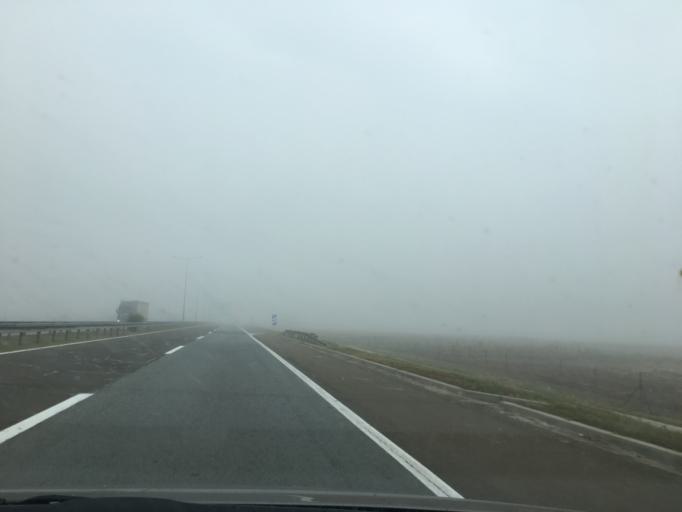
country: RS
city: Novi Karlovci
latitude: 45.0664
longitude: 20.1563
